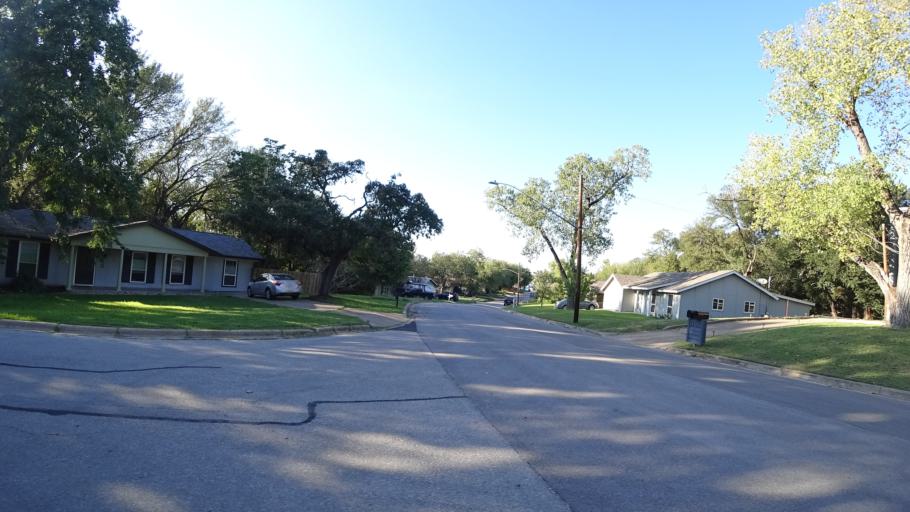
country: US
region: Texas
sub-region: Travis County
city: Austin
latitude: 30.2206
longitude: -97.7352
